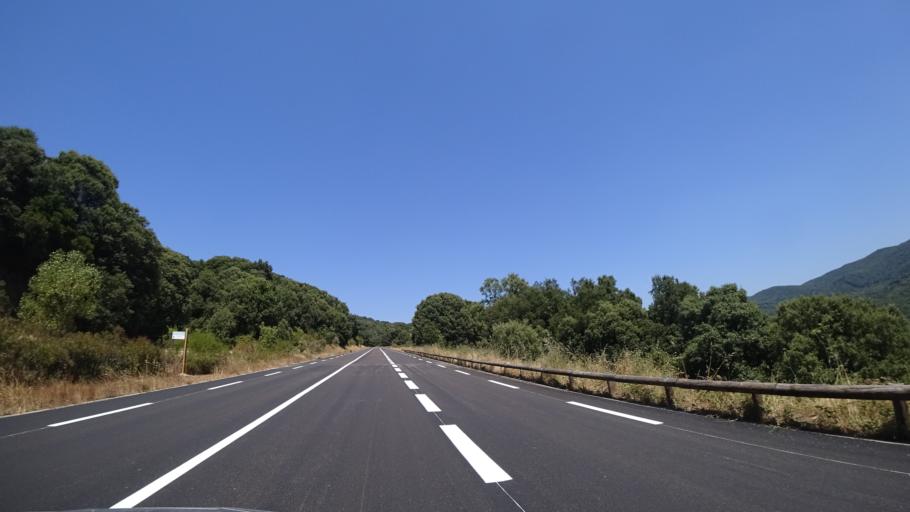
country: FR
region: Corsica
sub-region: Departement de la Corse-du-Sud
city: Grosseto-Prugna
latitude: 41.8585
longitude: 8.9613
